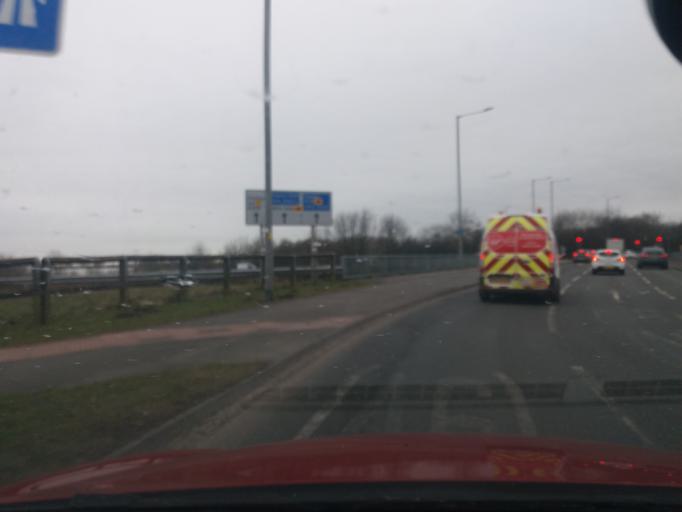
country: GB
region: England
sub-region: Lancashire
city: Chorley
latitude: 53.6701
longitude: -2.6240
